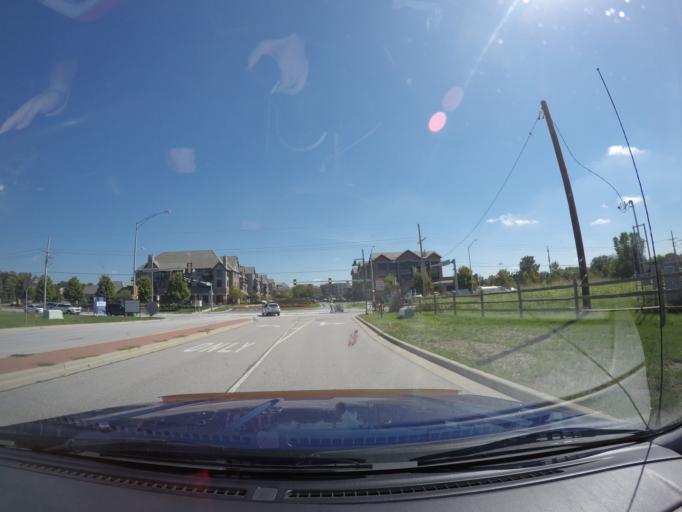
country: US
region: Kansas
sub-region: Johnson County
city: Leawood
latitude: 38.9343
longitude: -94.6308
